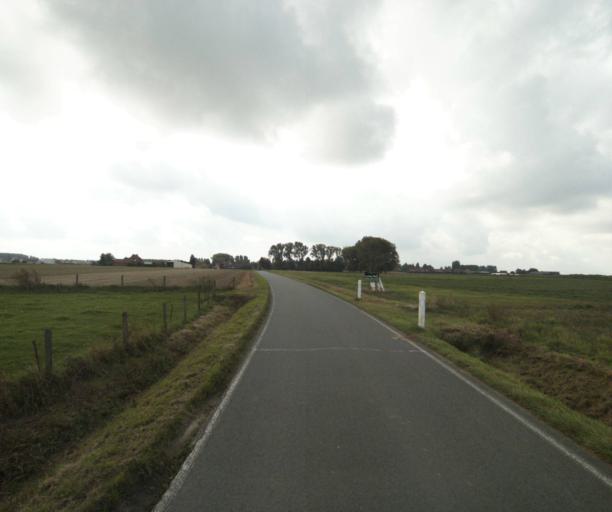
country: FR
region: Nord-Pas-de-Calais
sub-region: Departement du Nord
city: Herlies
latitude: 50.5871
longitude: 2.8504
